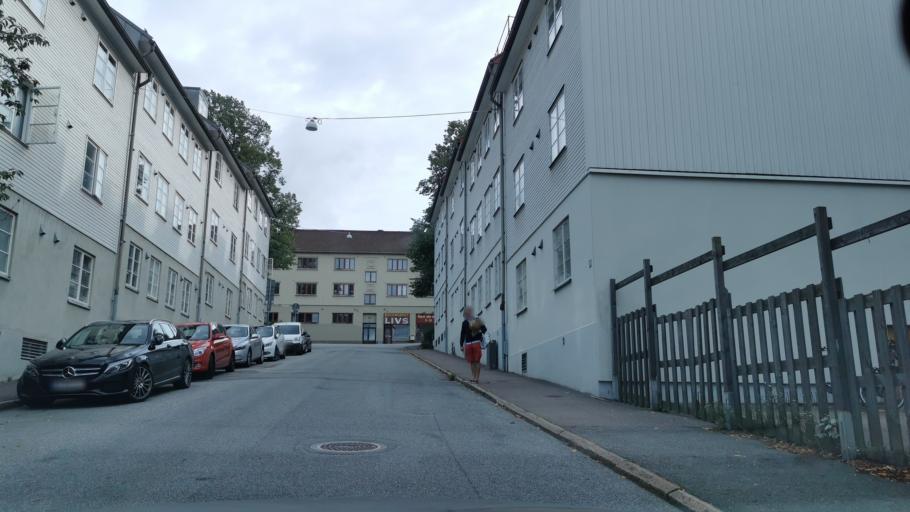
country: SE
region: Vaestra Goetaland
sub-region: Goteborg
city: Majorna
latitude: 57.6940
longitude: 11.9398
